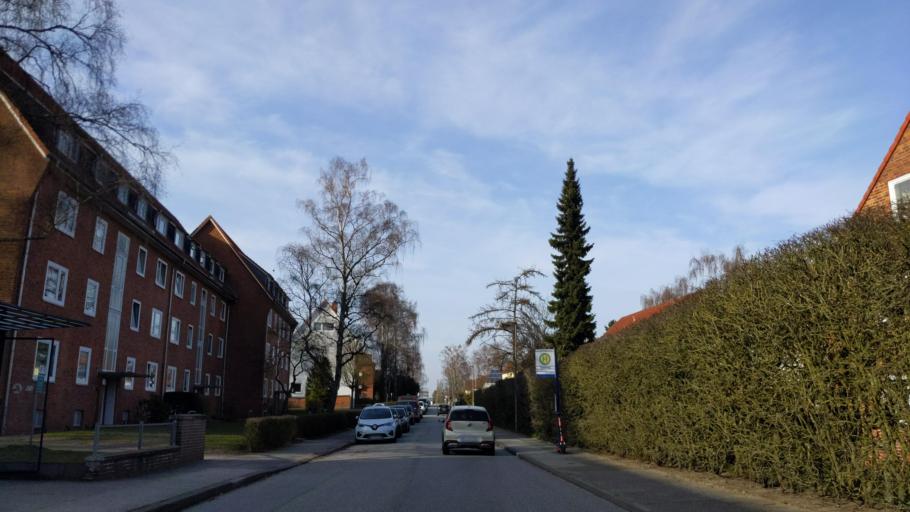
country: DE
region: Schleswig-Holstein
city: Bad Schwartau
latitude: 53.8903
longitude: 10.7112
